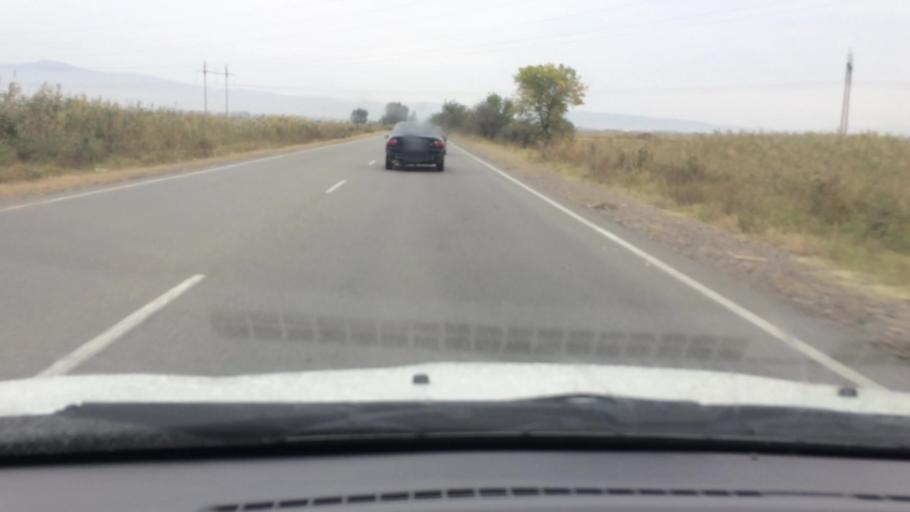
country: GE
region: Kvemo Kartli
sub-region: Marneuli
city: Marneuli
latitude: 41.5414
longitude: 44.7768
